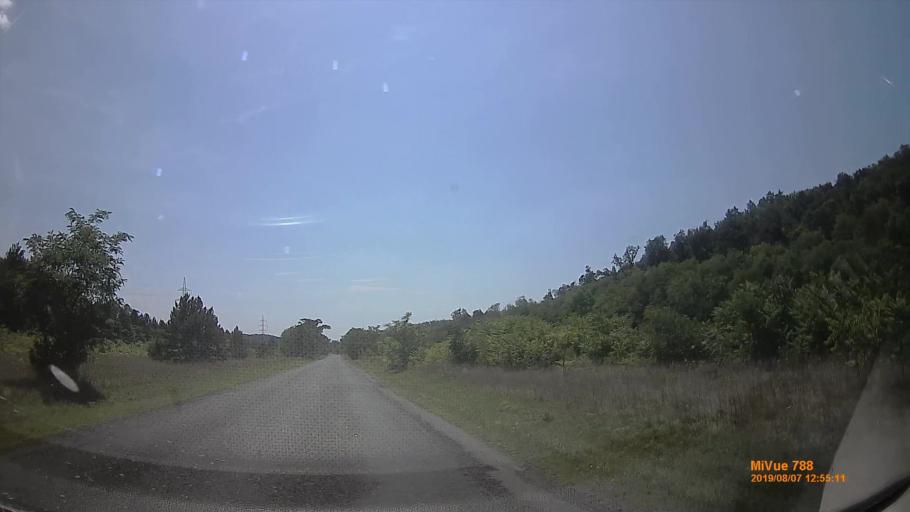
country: HU
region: Zala
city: Gyenesdias
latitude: 46.8140
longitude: 17.2703
